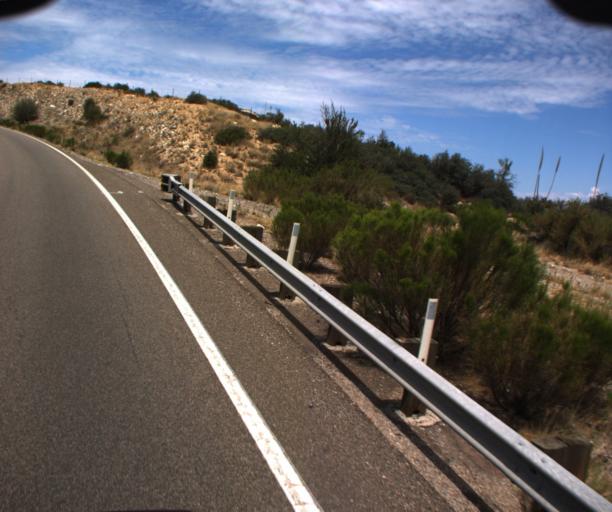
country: US
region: Arizona
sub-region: Gila County
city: Miami
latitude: 33.3654
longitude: -110.9618
